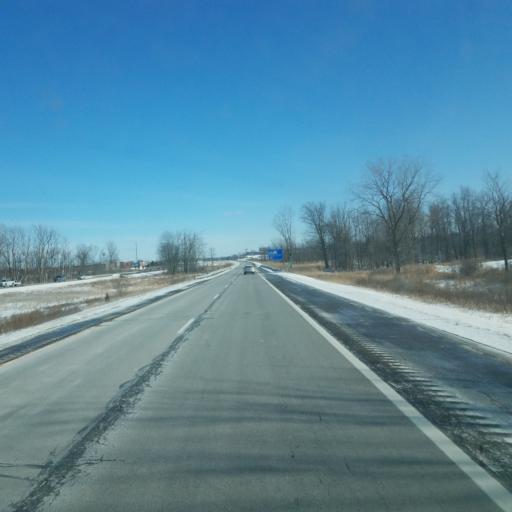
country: US
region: Michigan
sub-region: Livingston County
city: Fowlerville
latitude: 42.6460
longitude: -84.0848
